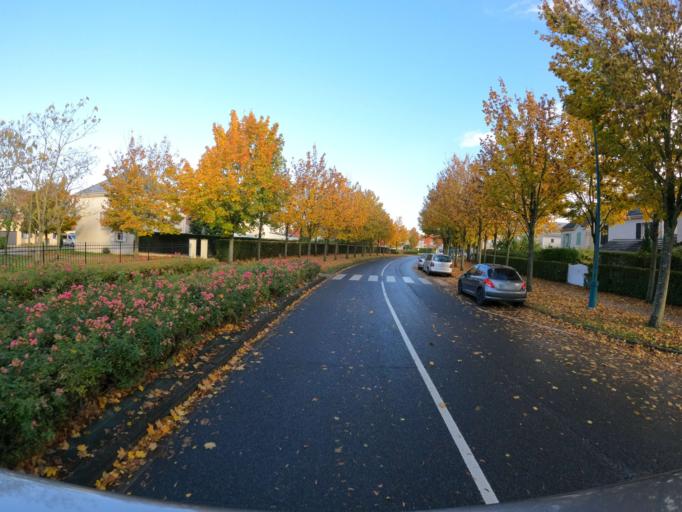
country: FR
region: Ile-de-France
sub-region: Departement de Seine-et-Marne
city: Bailly-Romainvilliers
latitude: 48.8468
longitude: 2.8159
